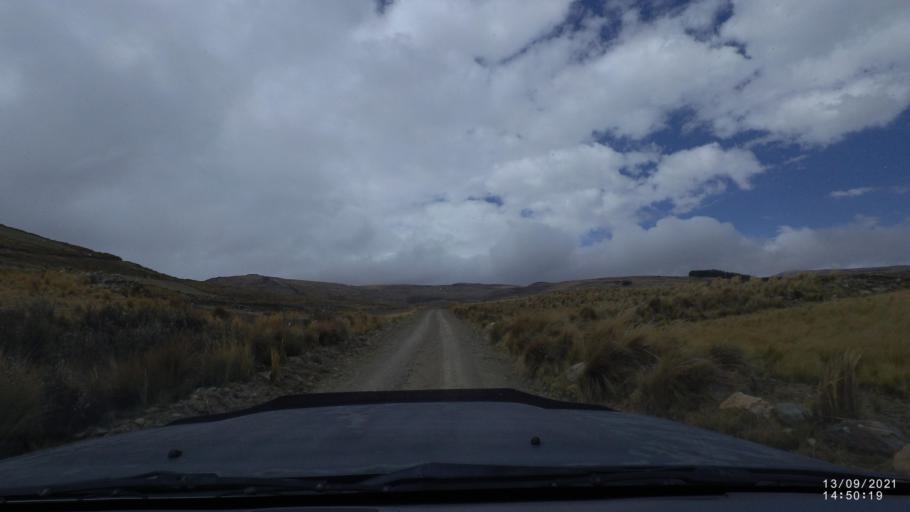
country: BO
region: Cochabamba
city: Colomi
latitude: -17.3475
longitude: -65.7958
